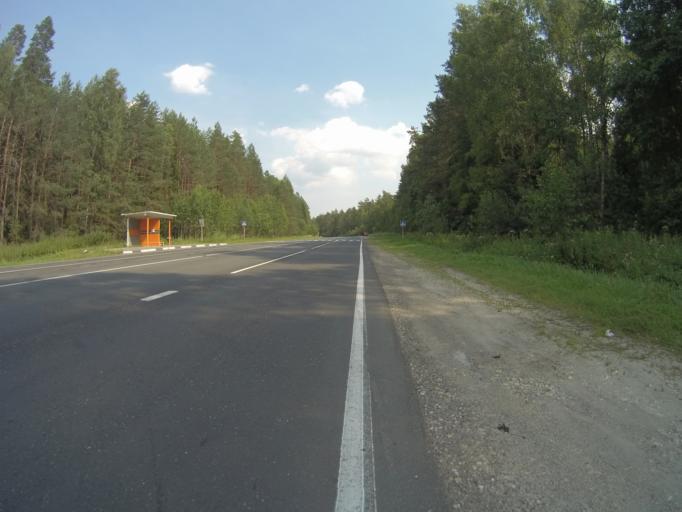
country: RU
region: Vladimir
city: Muromtsevo
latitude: 55.9533
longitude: 41.0049
